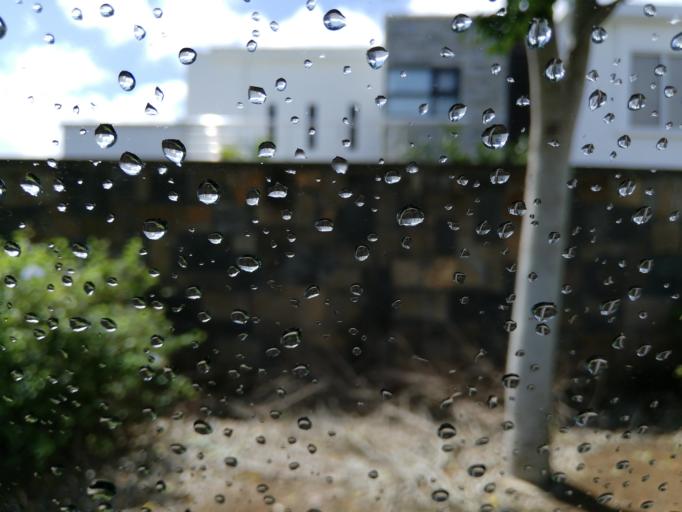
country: MU
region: Plaines Wilhems
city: Ebene
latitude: -20.2383
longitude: 57.4866
